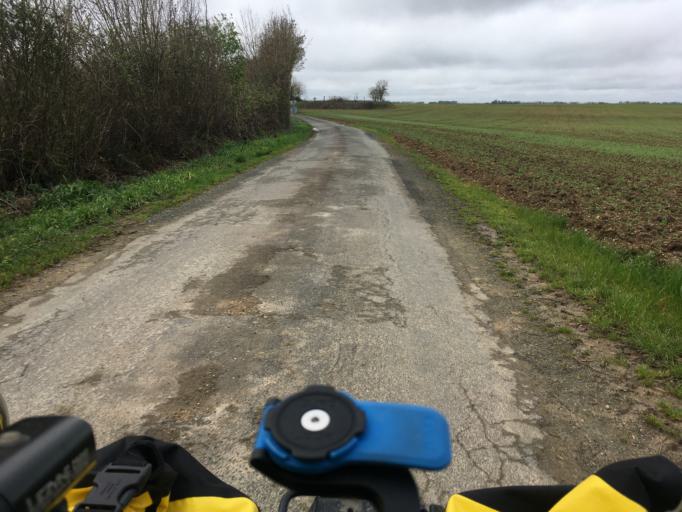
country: FR
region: Poitou-Charentes
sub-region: Departement de la Charente-Maritime
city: Saint-Germain-de-Marencennes
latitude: 46.1180
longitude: -0.8291
